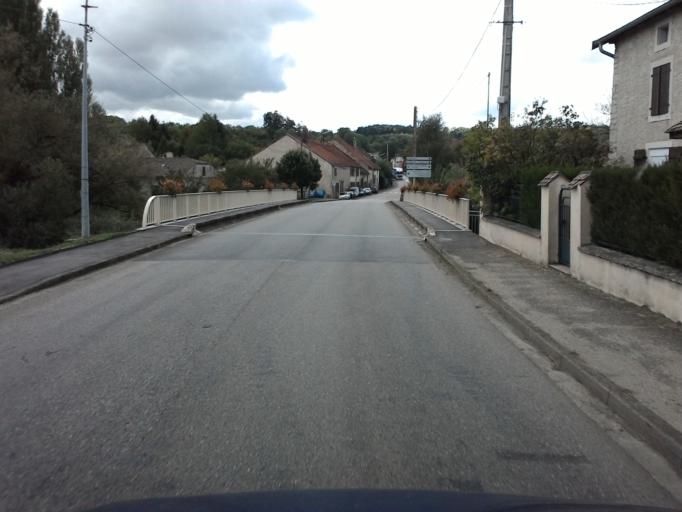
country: FR
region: Lorraine
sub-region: Departement des Vosges
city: Neufchateau
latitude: 48.4029
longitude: 5.7334
